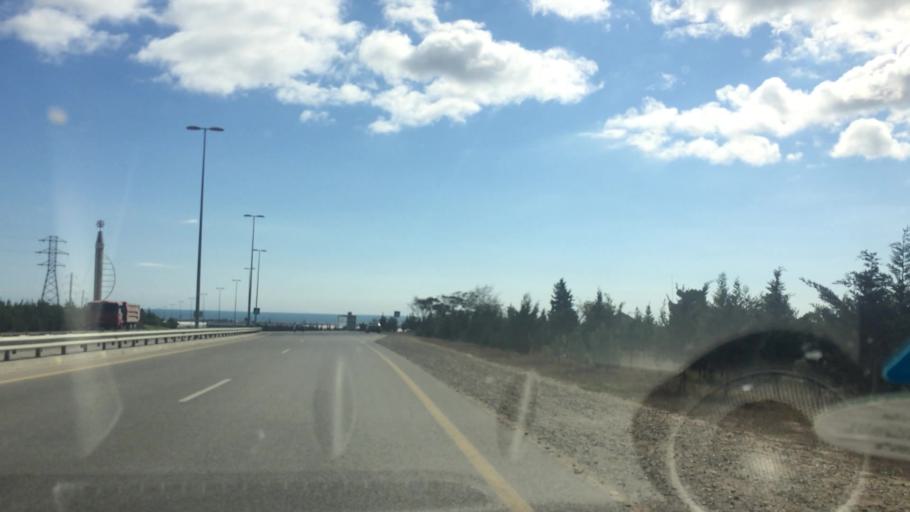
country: AZ
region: Baki
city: Zyrya
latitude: 40.4017
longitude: 50.3093
